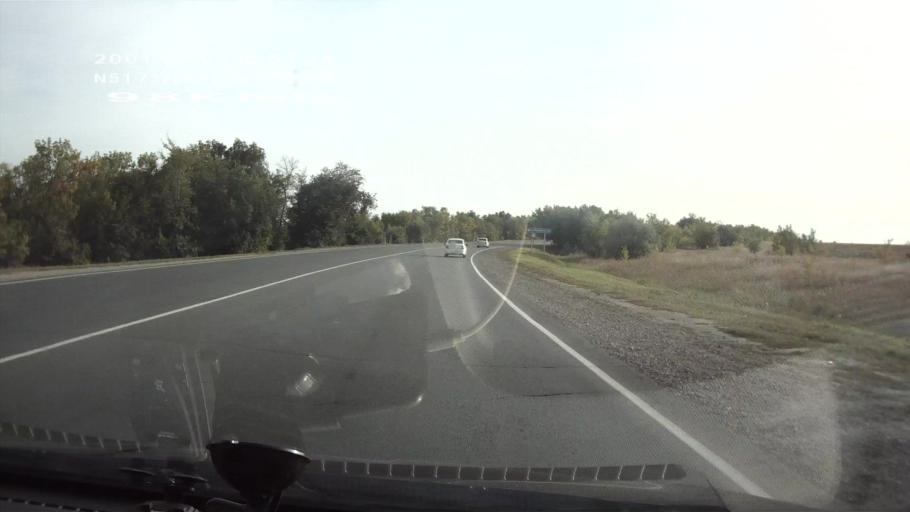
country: RU
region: Saratov
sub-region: Saratovskiy Rayon
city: Saratov
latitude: 51.7175
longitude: 46.0263
